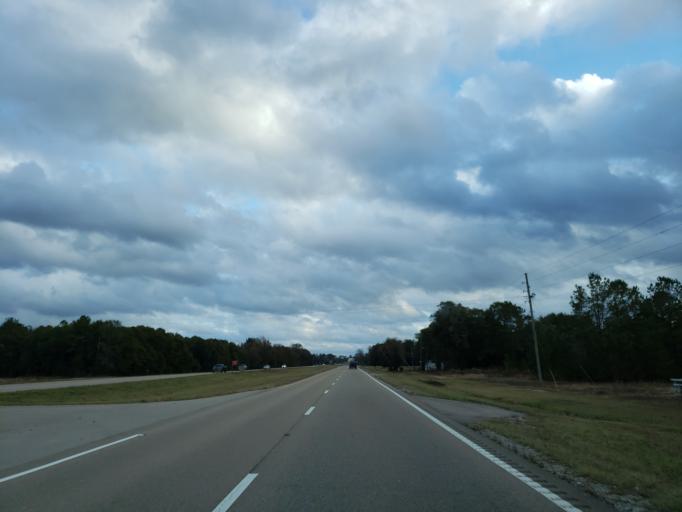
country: US
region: Mississippi
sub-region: Perry County
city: New Augusta
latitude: 31.1347
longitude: -88.8570
